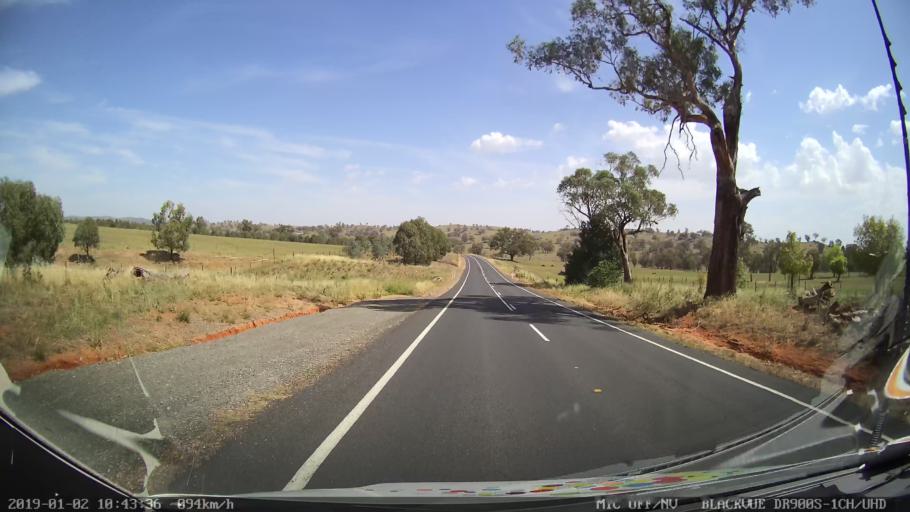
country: AU
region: New South Wales
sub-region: Cootamundra
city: Cootamundra
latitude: -34.7704
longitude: 148.3030
